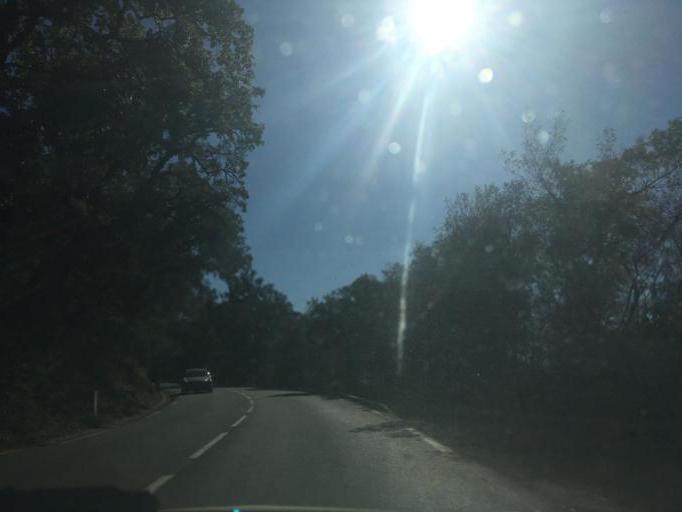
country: FR
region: Provence-Alpes-Cote d'Azur
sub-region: Departement du Var
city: Grimaud
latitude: 43.2749
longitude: 6.5165
